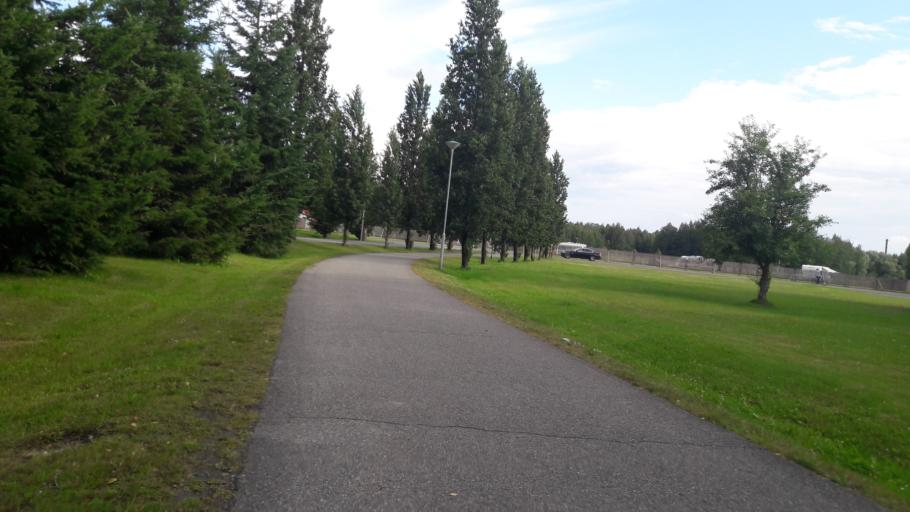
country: FI
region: North Karelia
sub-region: Joensuu
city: Joensuu
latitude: 62.5923
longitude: 29.7401
